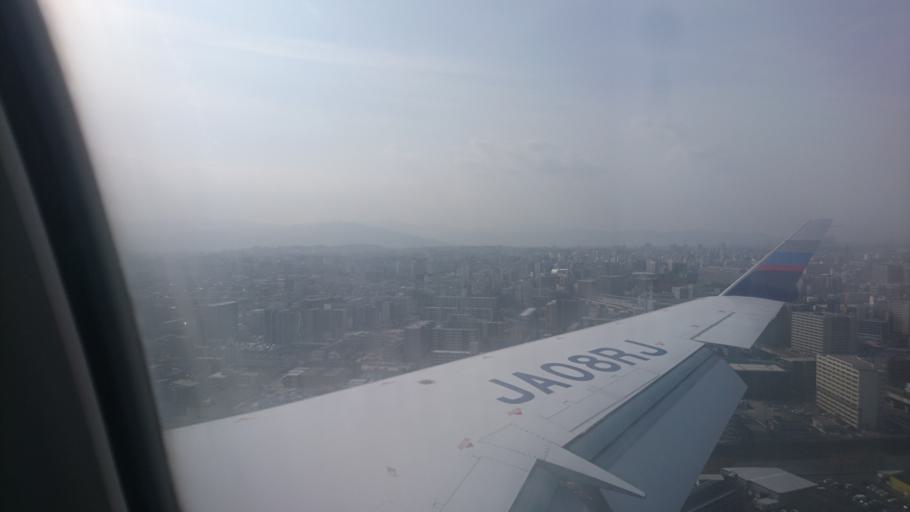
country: JP
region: Fukuoka
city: Fukuoka-shi
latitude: 33.6114
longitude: 130.4331
